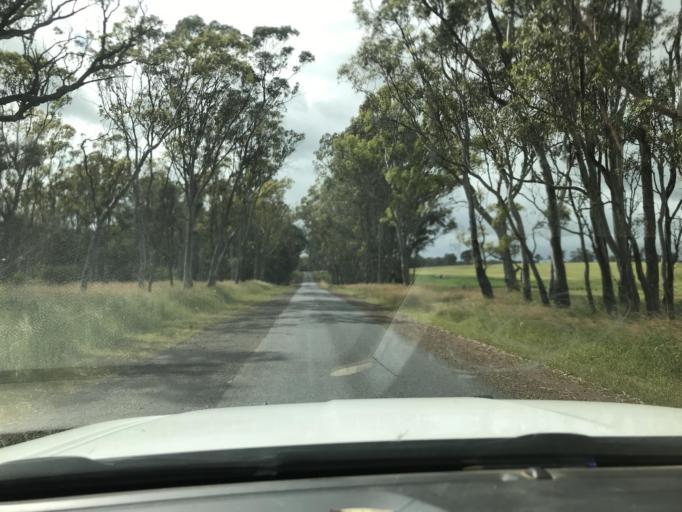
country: AU
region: South Australia
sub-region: Wattle Range
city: Penola
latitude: -37.1678
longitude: 141.4224
